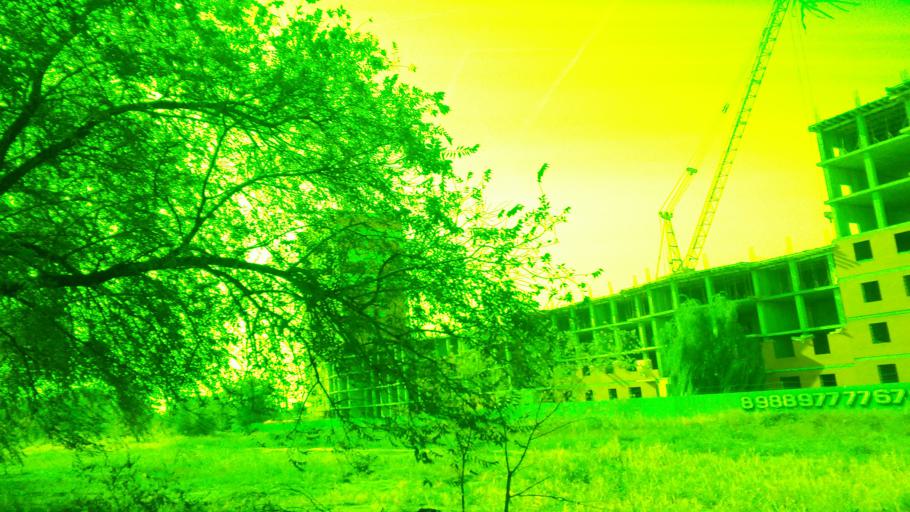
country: RU
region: Volgograd
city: Vodstroy
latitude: 48.8378
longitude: 44.6463
